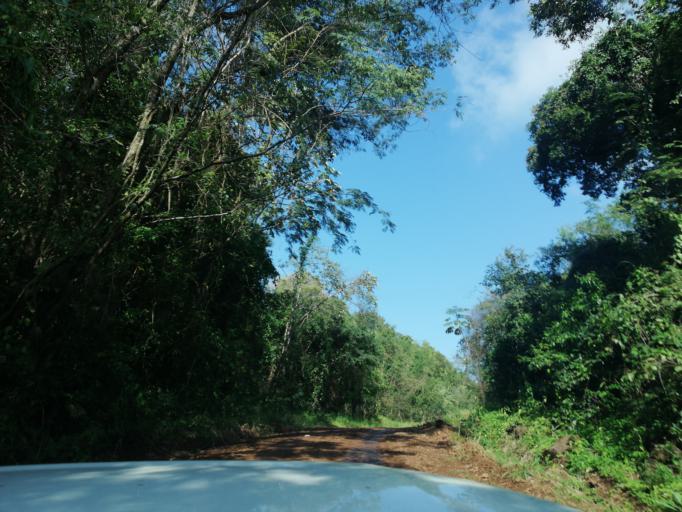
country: AR
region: Misiones
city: Cerro Azul
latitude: -27.6184
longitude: -55.5236
